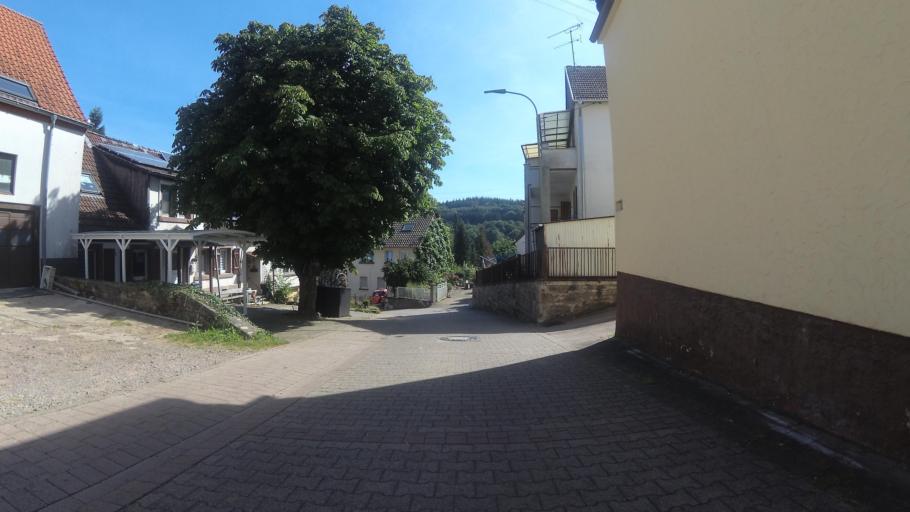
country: DE
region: Rheinland-Pfalz
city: Dunzweiler
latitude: 49.4144
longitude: 7.3070
